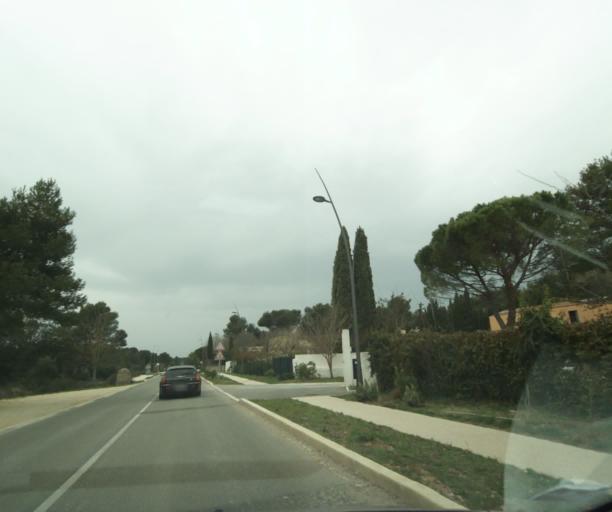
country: FR
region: Provence-Alpes-Cote d'Azur
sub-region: Departement des Bouches-du-Rhone
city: Saint-Marc-Jaumegarde
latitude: 43.5462
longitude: 5.5156
